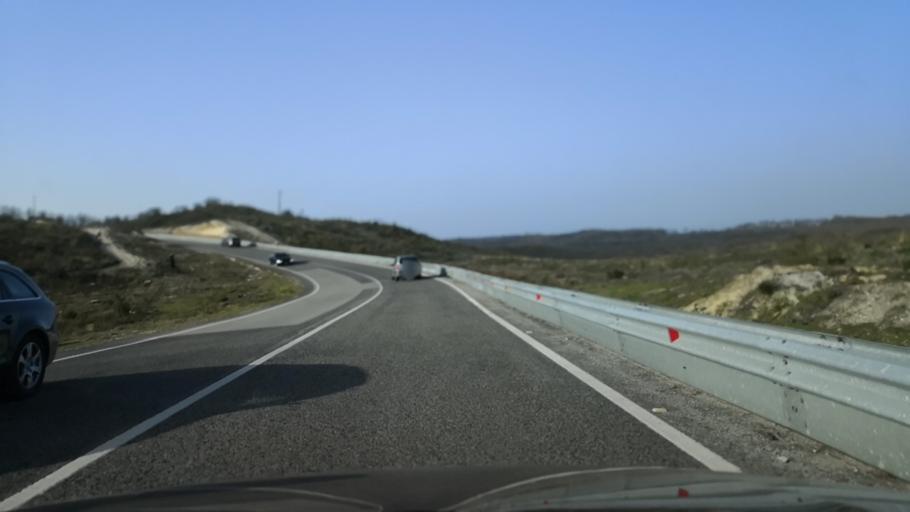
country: PT
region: Leiria
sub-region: Marinha Grande
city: Marinha Grande
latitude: 39.7437
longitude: -8.9833
